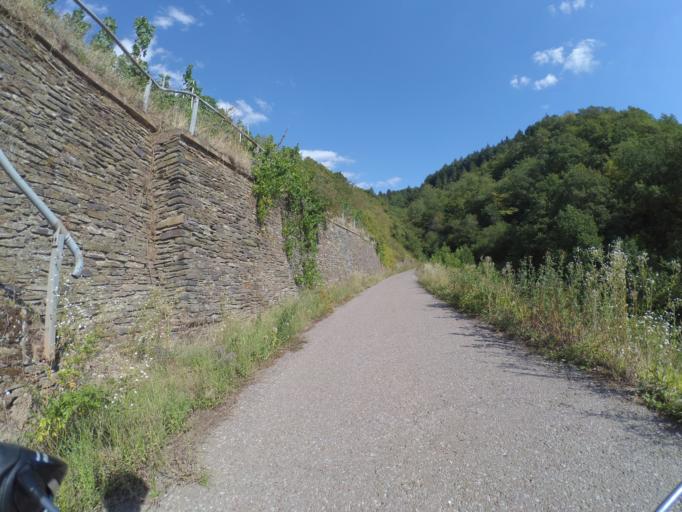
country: DE
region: Rheinland-Pfalz
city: Longuich
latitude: 49.8145
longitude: 6.7733
